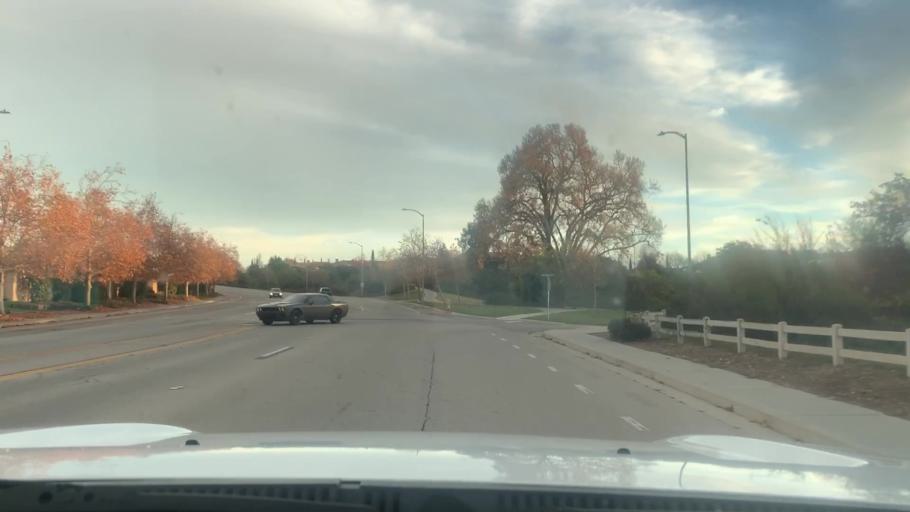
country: US
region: California
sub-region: San Luis Obispo County
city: Paso Robles
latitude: 35.6344
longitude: -120.6582
